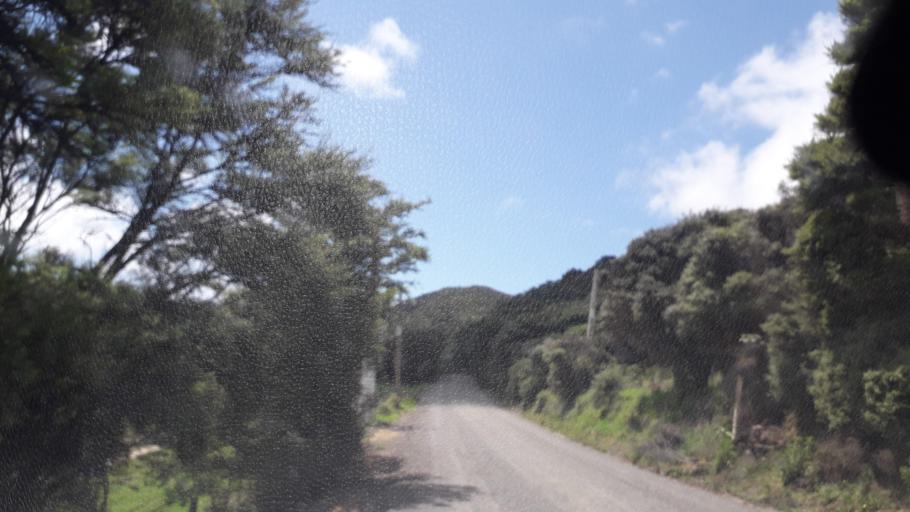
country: NZ
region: Northland
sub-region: Far North District
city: Paihia
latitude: -35.2625
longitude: 174.2644
